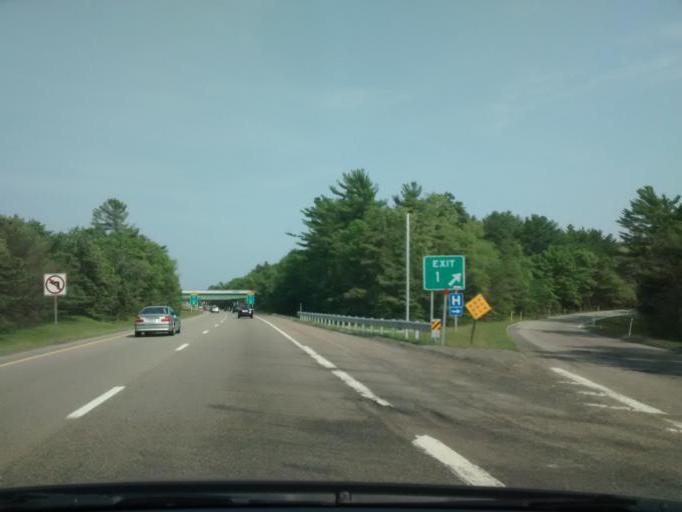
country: US
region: Massachusetts
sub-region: Plymouth County
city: Wareham Center
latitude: 41.7847
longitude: -70.7348
